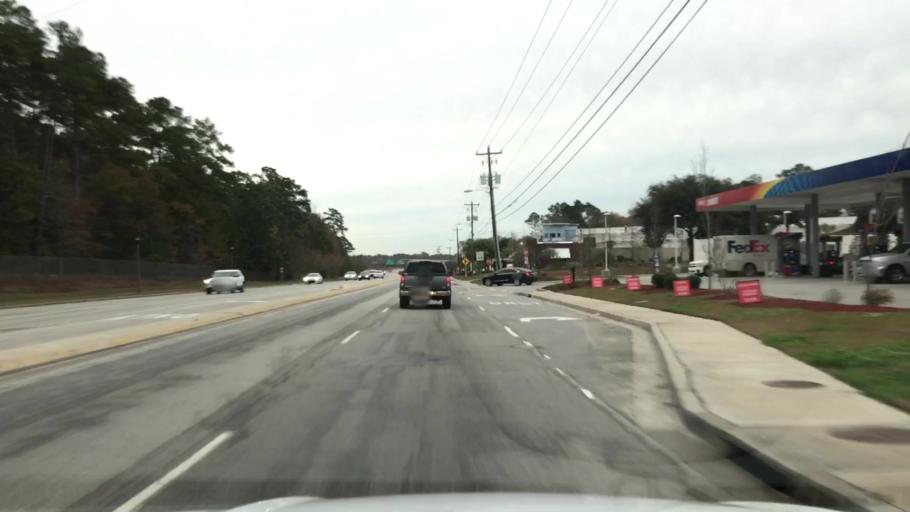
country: US
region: South Carolina
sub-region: Berkeley County
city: Goose Creek
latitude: 32.9744
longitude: -80.0592
